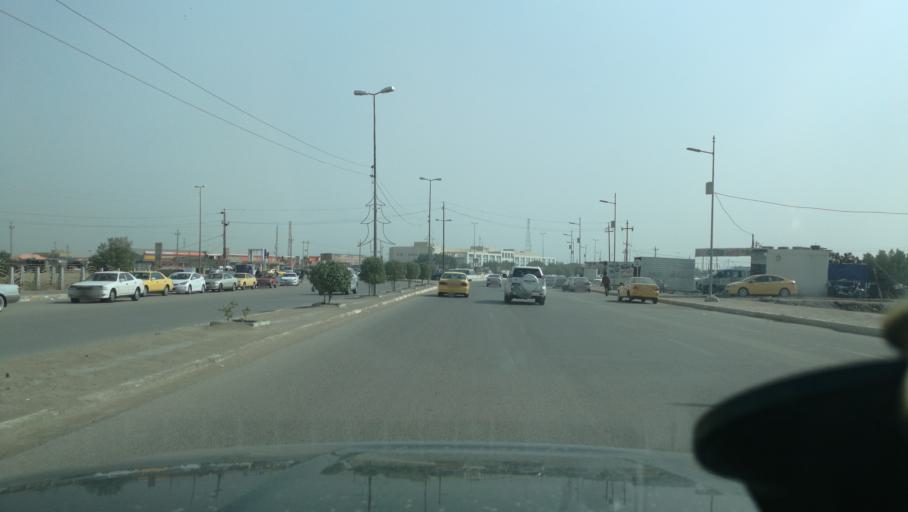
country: IQ
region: Dhi Qar
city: An Nasiriyah
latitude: 31.0838
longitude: 46.2454
